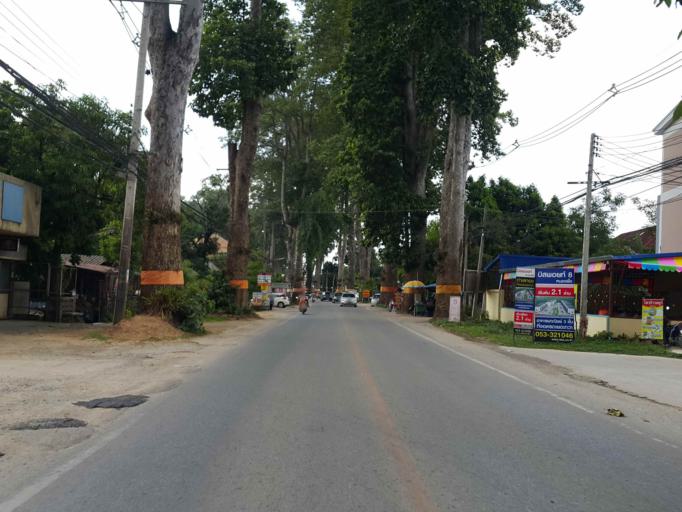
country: TH
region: Chiang Mai
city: Saraphi
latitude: 18.7213
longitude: 99.0267
